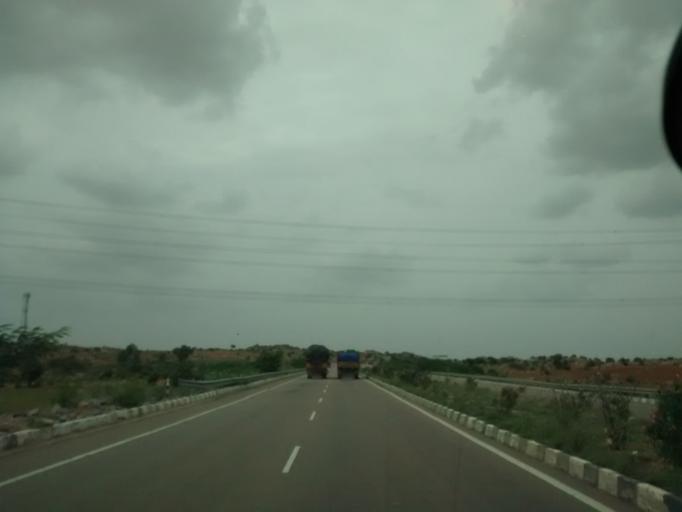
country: IN
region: Andhra Pradesh
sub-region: Kurnool
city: Ramapuram
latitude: 15.1507
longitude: 77.6663
